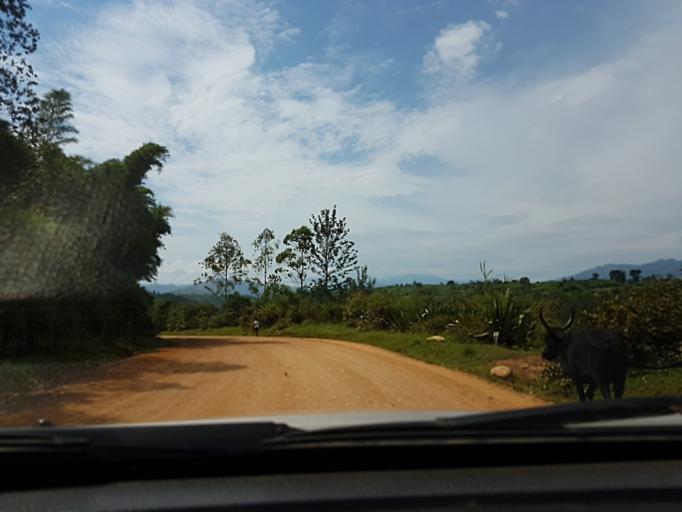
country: CD
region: South Kivu
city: Bukavu
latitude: -2.6262
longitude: 28.8741
